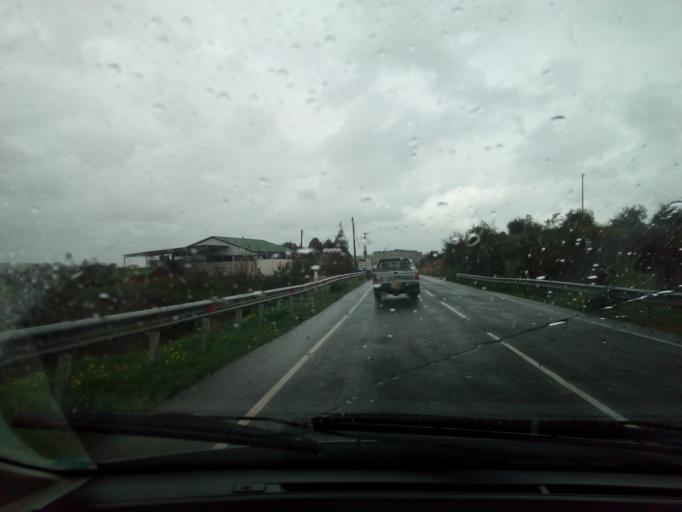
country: CY
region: Pafos
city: Polis
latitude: 35.0000
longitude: 32.4449
